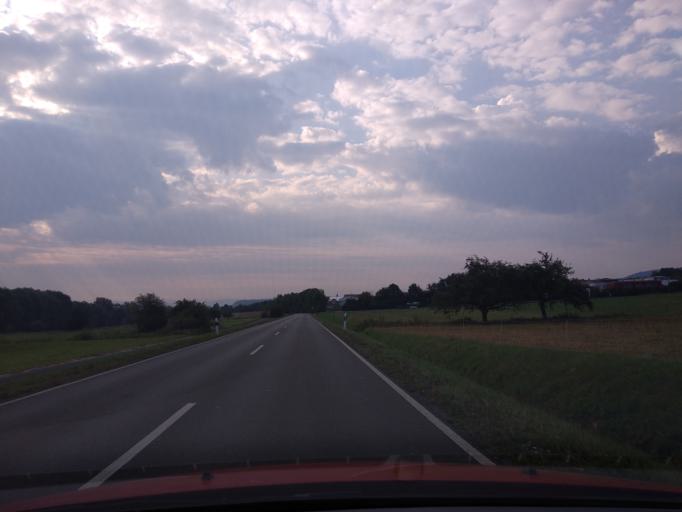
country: DE
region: Hesse
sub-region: Regierungsbezirk Kassel
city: Calden
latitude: 51.3741
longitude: 9.3840
